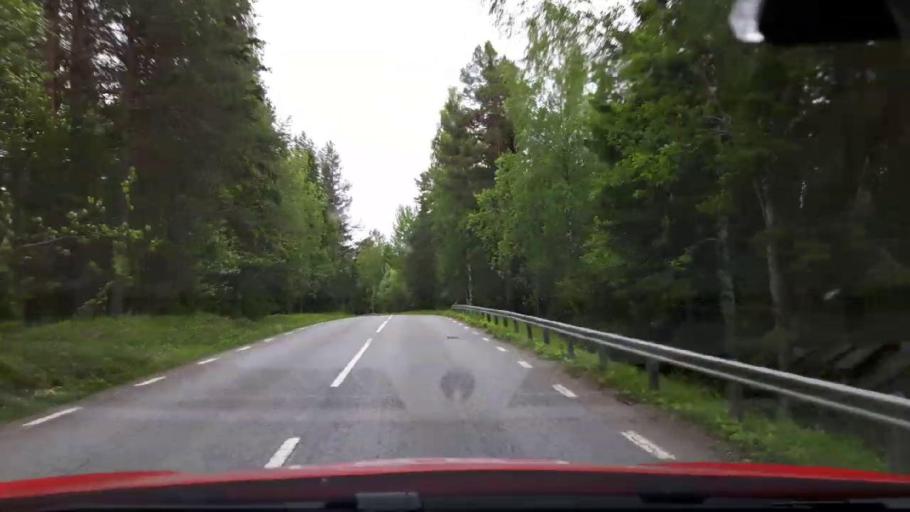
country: SE
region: Jaemtland
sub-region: Stroemsunds Kommun
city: Stroemsund
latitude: 63.5262
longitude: 15.4559
